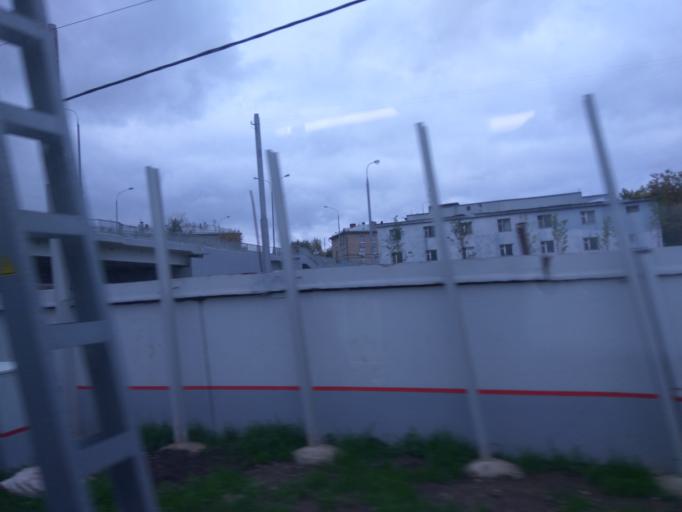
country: RU
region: Moscow
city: Sokol
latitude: 55.7711
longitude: 37.5131
